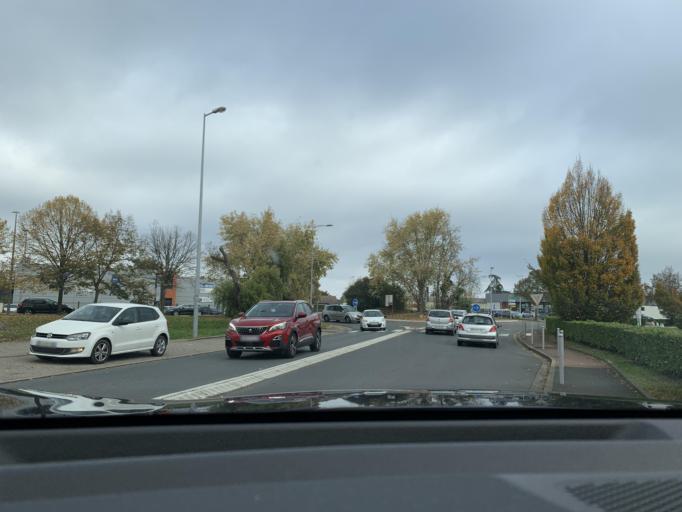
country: FR
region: Rhone-Alpes
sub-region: Departement du Rhone
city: Lozanne
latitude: 45.8566
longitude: 4.7047
